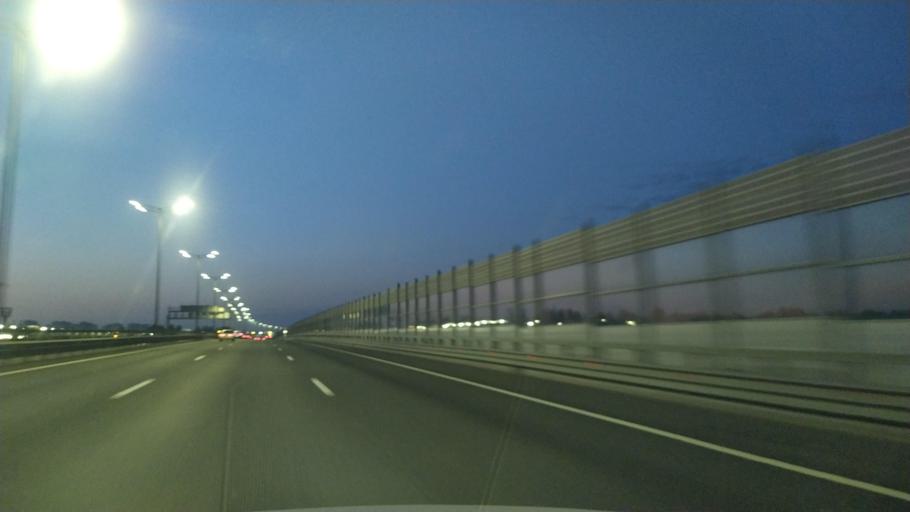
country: RU
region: St.-Petersburg
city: Pargolovo
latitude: 60.0902
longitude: 30.2409
